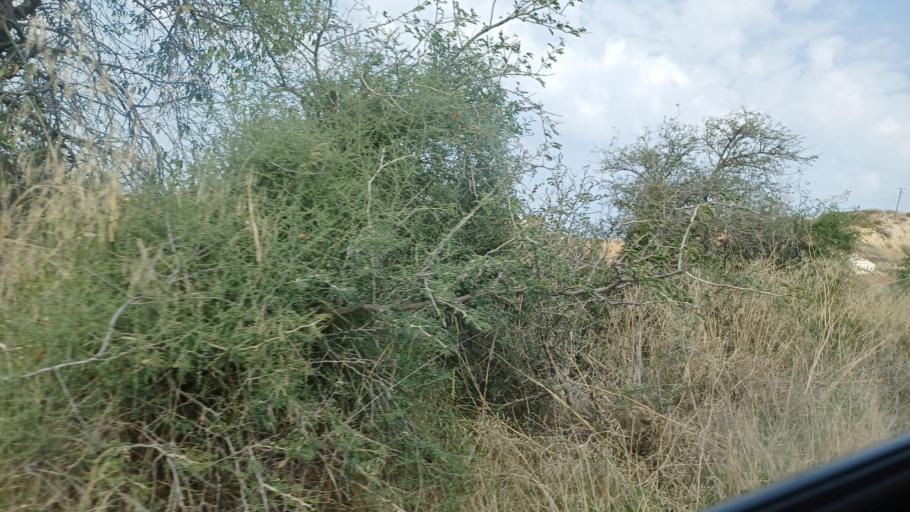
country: CY
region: Pafos
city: Polis
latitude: 34.9857
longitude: 32.4545
